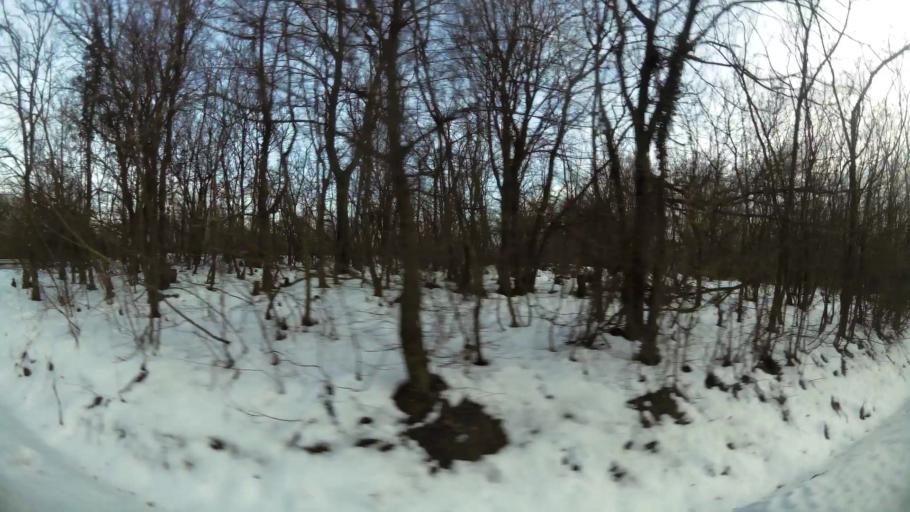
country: RS
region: Central Serbia
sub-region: Belgrade
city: Zvezdara
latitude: 44.7284
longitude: 20.5062
